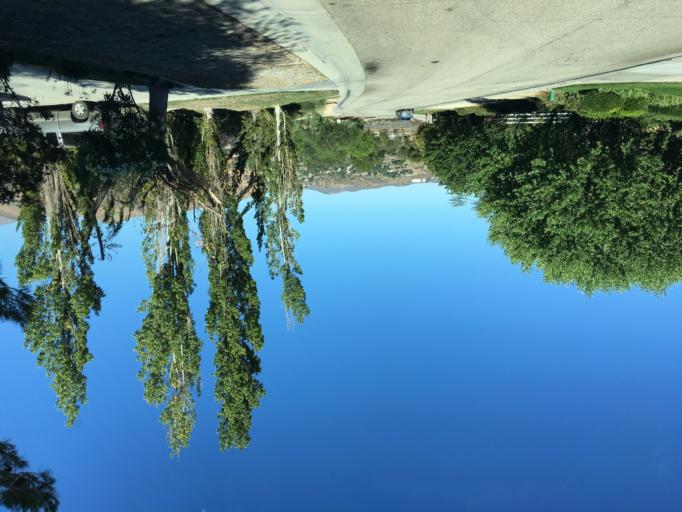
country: US
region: California
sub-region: Los Angeles County
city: Acton
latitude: 34.4711
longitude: -118.1568
